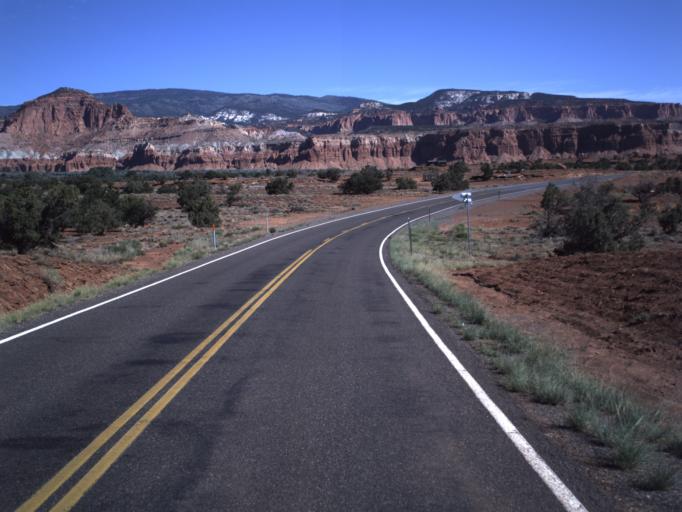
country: US
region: Utah
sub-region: Wayne County
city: Loa
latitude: 38.3031
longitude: -111.3927
